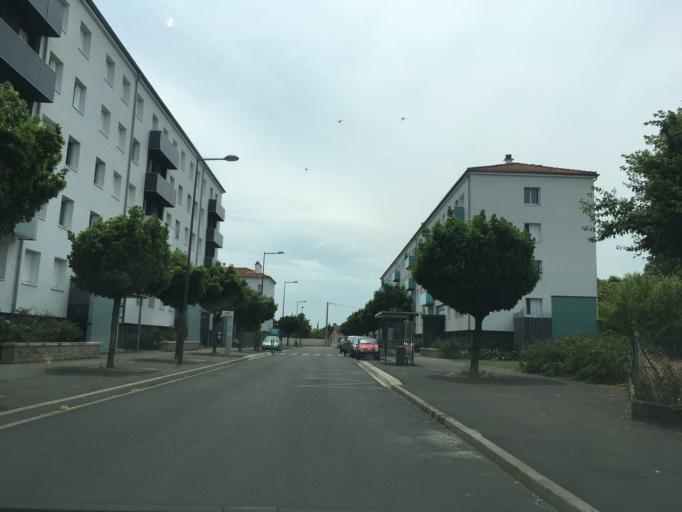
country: FR
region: Poitou-Charentes
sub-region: Departement des Deux-Sevres
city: Niort
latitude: 46.3264
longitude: -0.4803
